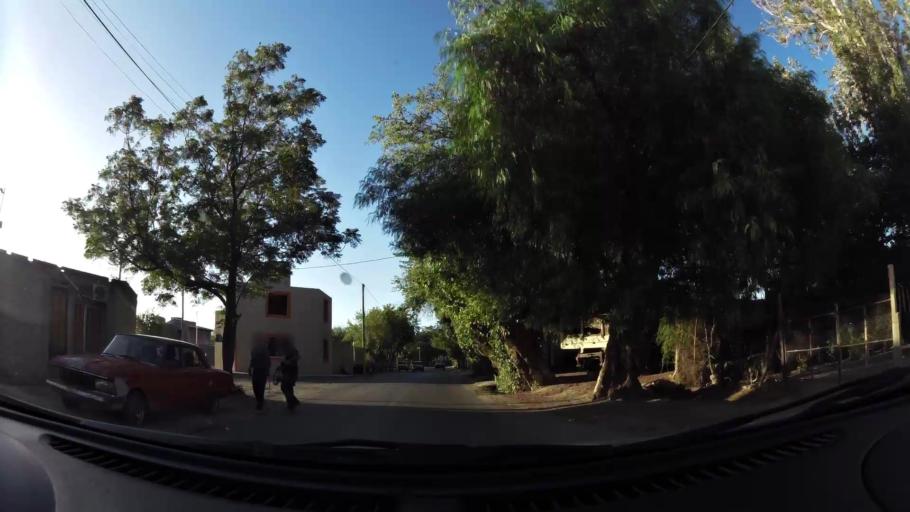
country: AR
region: San Juan
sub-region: Departamento de Santa Lucia
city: Santa Lucia
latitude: -31.5520
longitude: -68.4760
